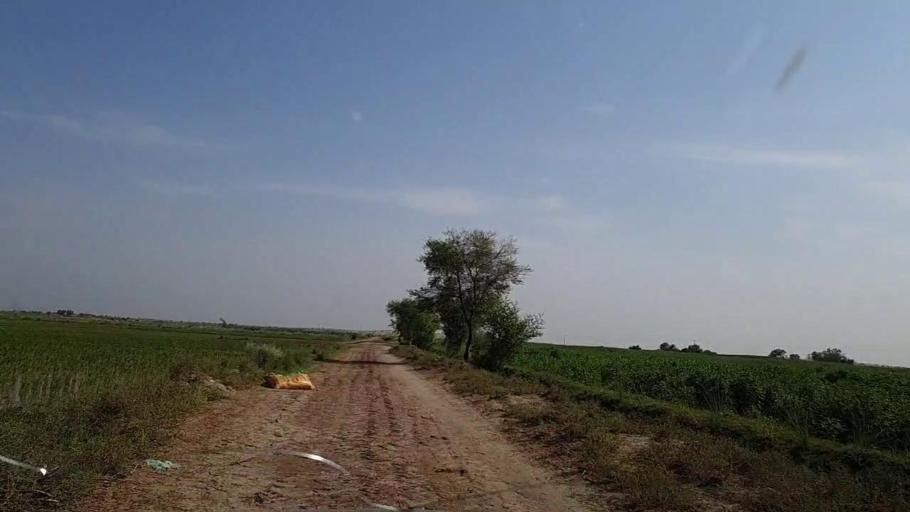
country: PK
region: Sindh
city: Khanpur
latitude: 27.6895
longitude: 69.3675
